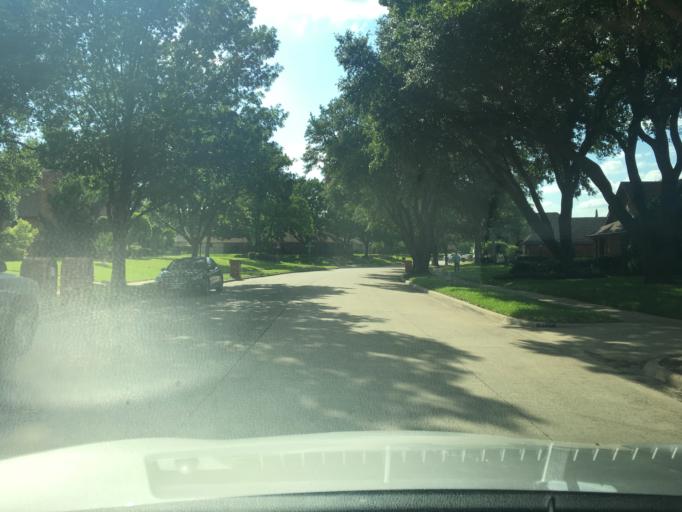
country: US
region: Texas
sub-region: Dallas County
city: Garland
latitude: 32.9388
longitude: -96.6767
